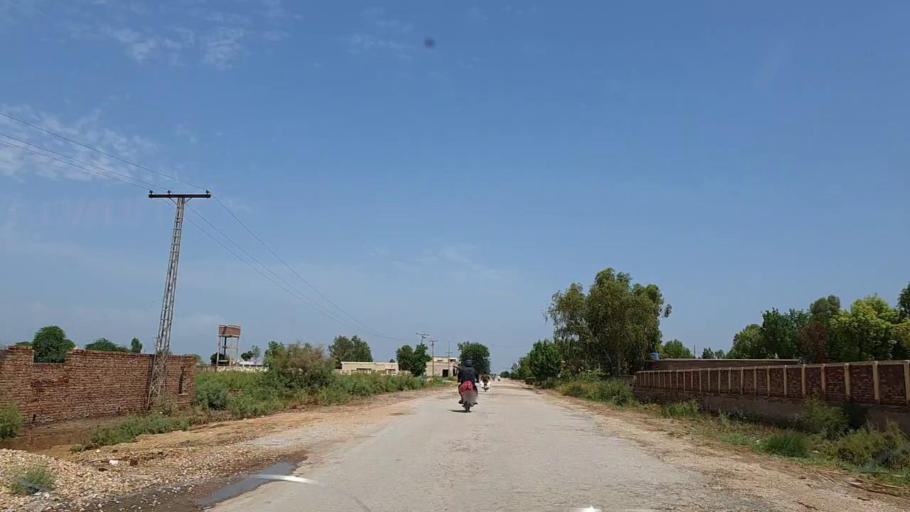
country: PK
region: Sindh
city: Naushahro Firoz
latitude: 26.8306
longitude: 68.1398
